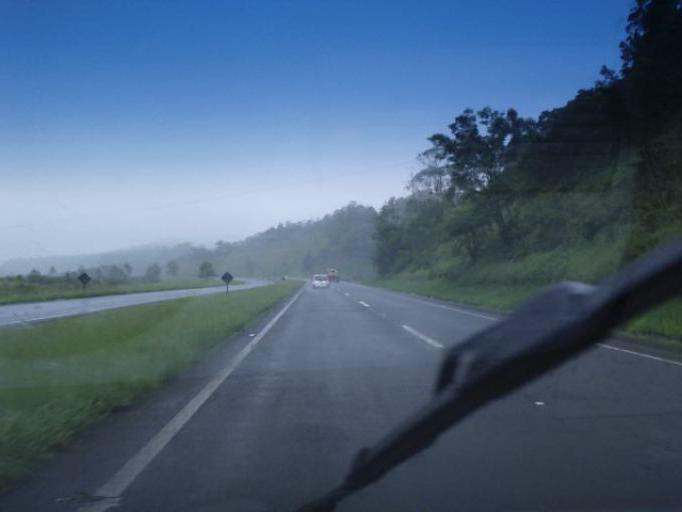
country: BR
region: Parana
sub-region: Antonina
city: Antonina
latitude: -25.0977
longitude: -48.6571
